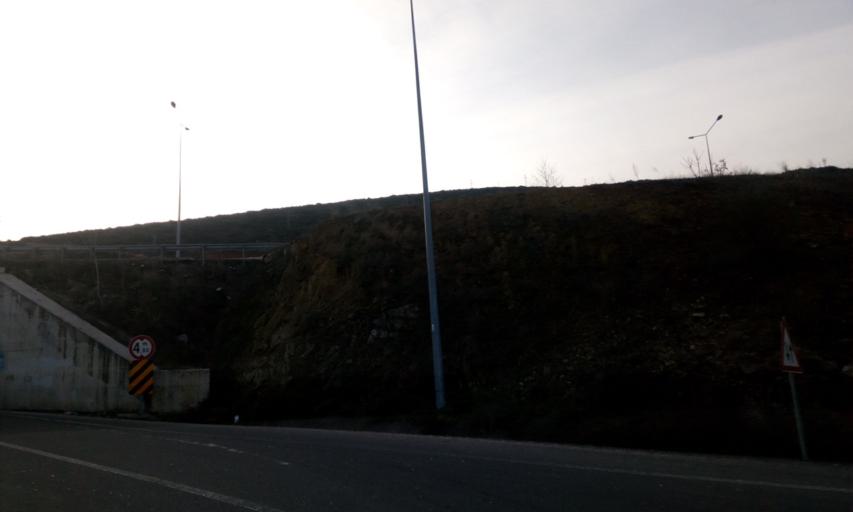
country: TR
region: Bilecik
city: Kuplu
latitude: 40.1209
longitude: 30.0110
